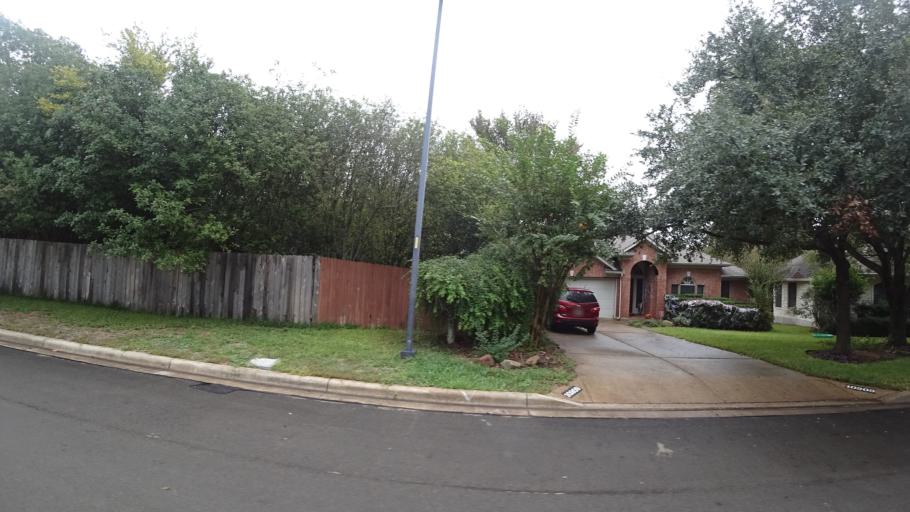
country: US
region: Texas
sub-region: Travis County
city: Shady Hollow
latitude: 30.1881
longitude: -97.8661
